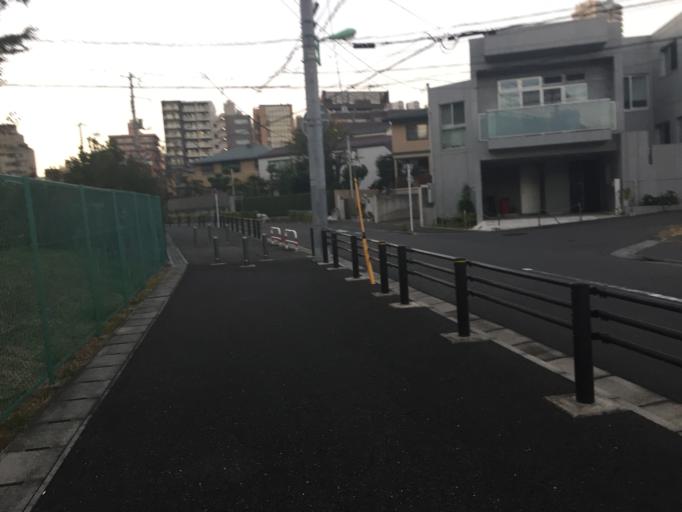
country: JP
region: Tokyo
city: Tokyo
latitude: 35.6296
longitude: 139.6595
